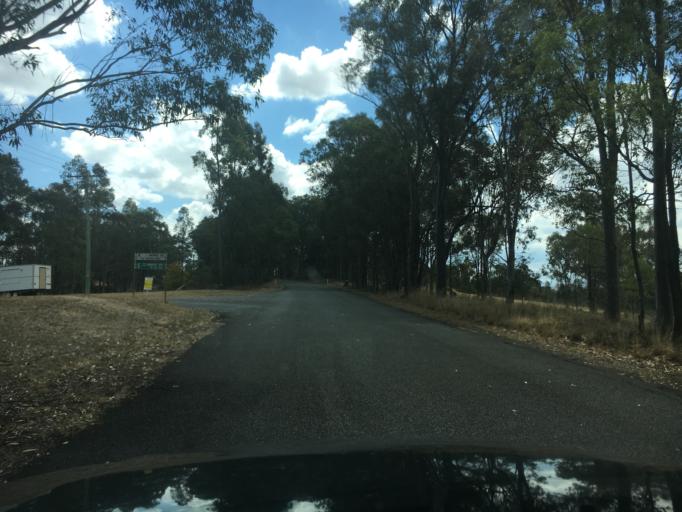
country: AU
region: New South Wales
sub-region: Singleton
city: Singleton
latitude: -32.5273
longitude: 151.1998
